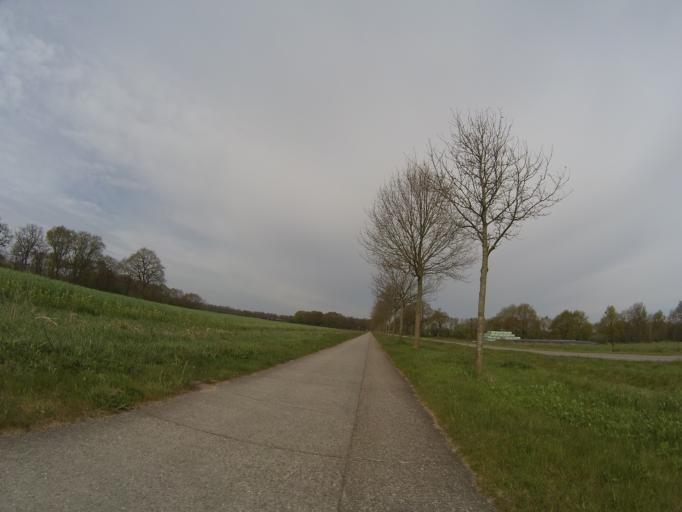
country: NL
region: Drenthe
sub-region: Gemeente Coevorden
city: Sleen
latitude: 52.8384
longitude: 6.6687
